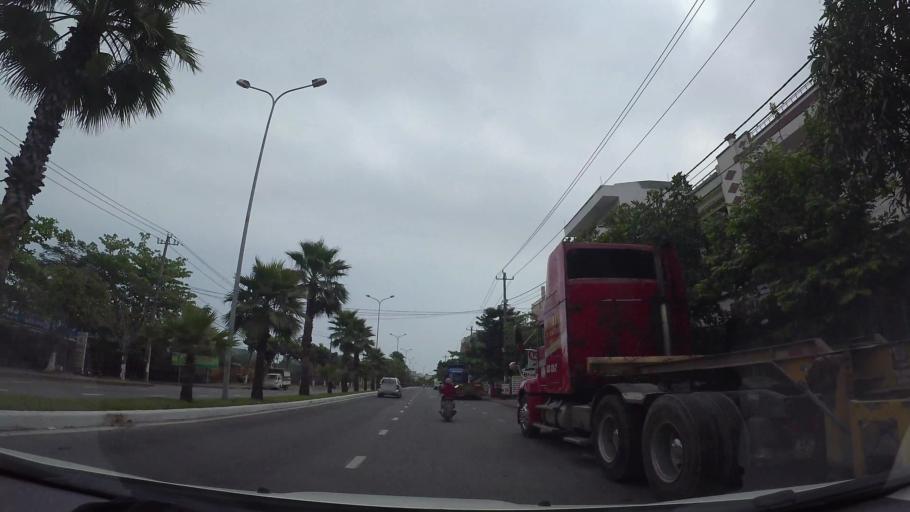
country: VN
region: Da Nang
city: Da Nang
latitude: 16.1045
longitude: 108.2469
